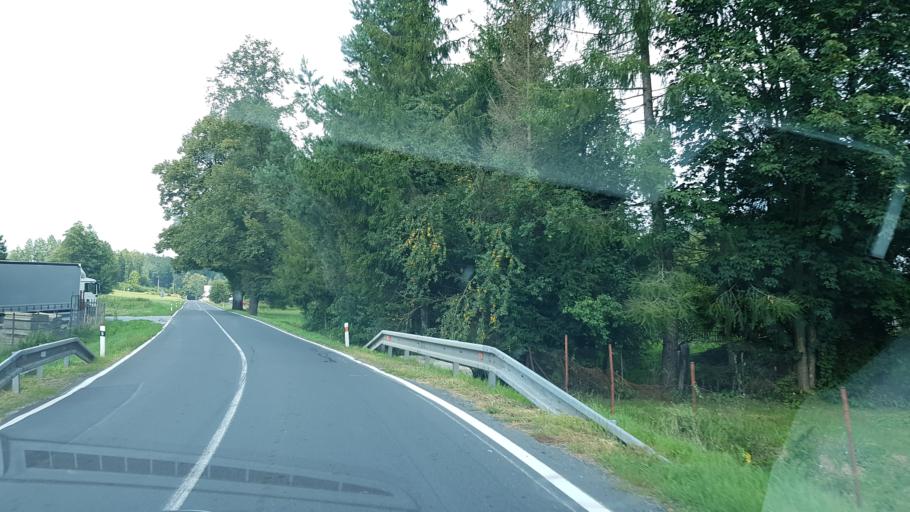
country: CZ
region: Olomoucky
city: Mikulovice
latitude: 50.2780
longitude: 17.3429
